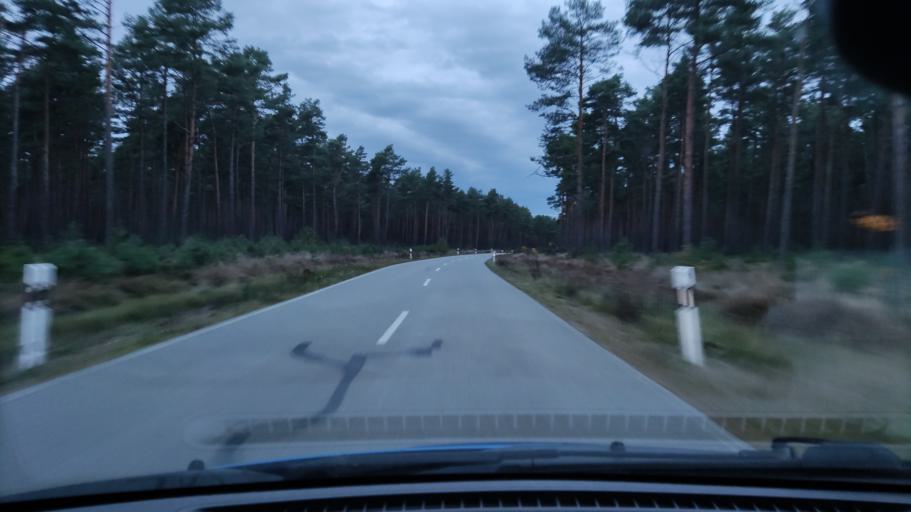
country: DE
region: Lower Saxony
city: Prezelle
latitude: 52.9936
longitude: 11.3945
